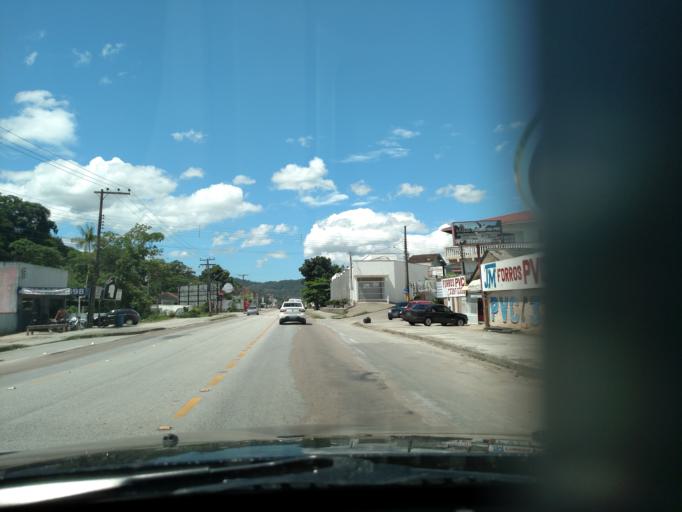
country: BR
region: Santa Catarina
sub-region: Blumenau
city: Blumenau
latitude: -26.8997
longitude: -49.0103
